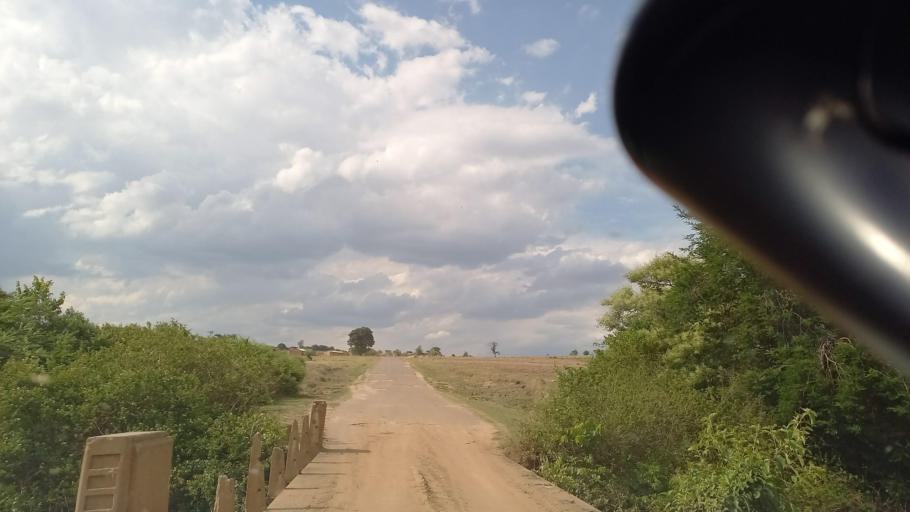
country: ZM
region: Lusaka
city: Kafue
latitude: -16.2092
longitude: 28.1115
